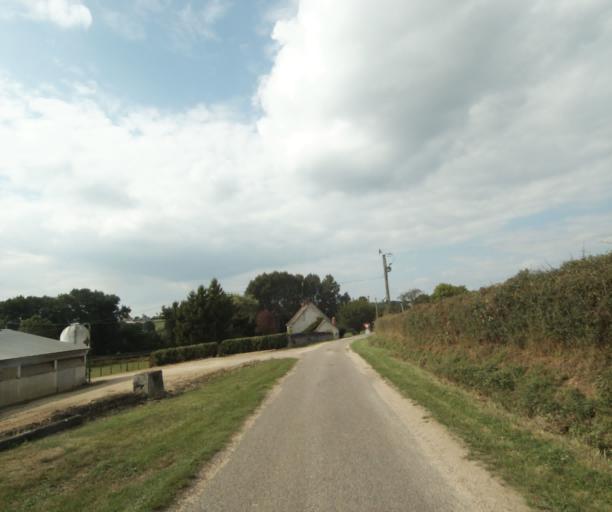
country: FR
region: Bourgogne
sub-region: Departement de Saone-et-Loire
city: Palinges
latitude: 46.5048
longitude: 4.1876
